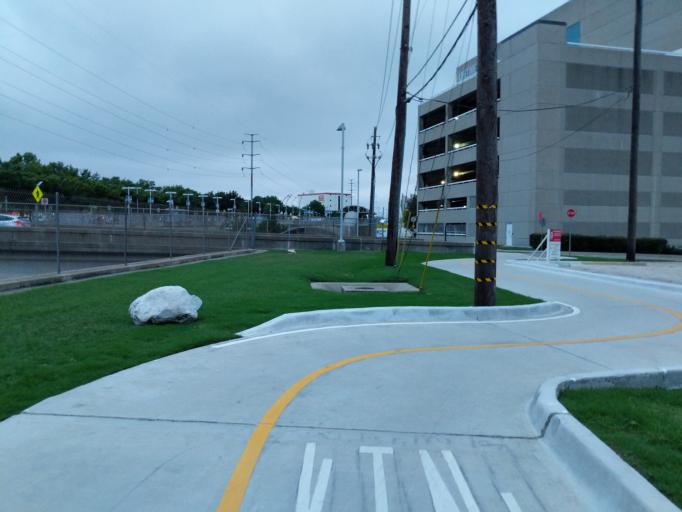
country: US
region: Texas
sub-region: Dallas County
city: Highland Park
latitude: 32.8389
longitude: -96.7739
